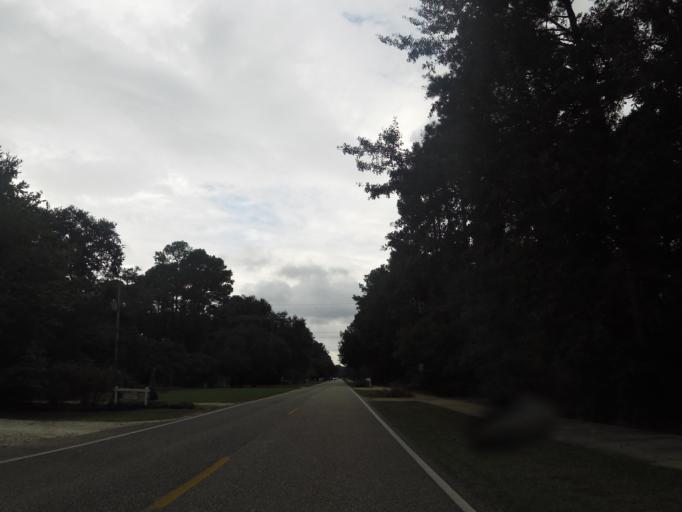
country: US
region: Alabama
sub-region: Baldwin County
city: Point Clear
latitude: 30.4309
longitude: -87.9105
